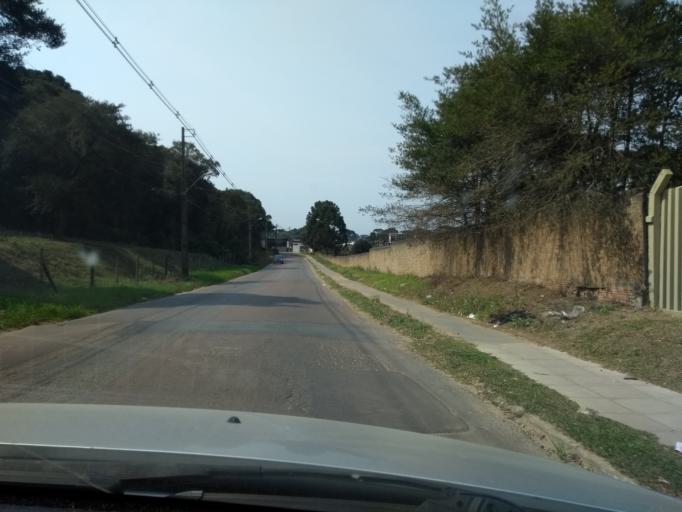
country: BR
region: Parana
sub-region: Araucaria
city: Araucaria
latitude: -25.6030
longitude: -49.3209
